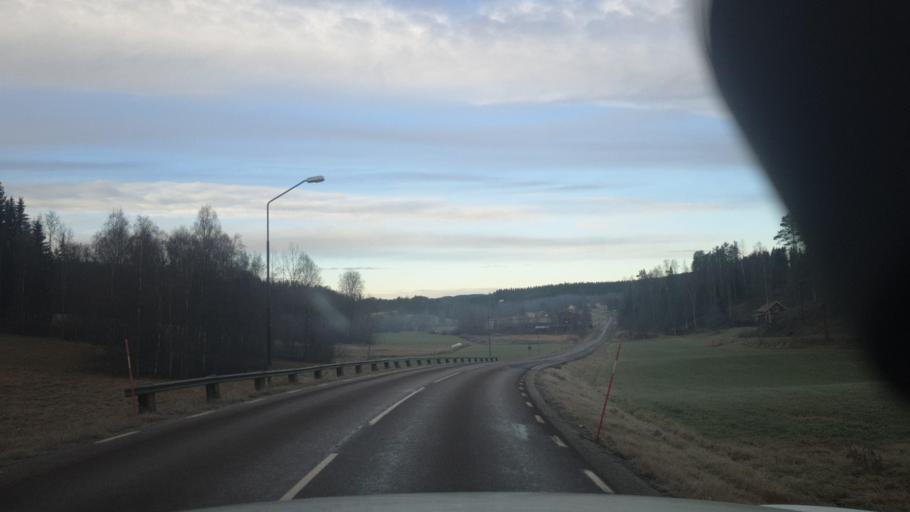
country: SE
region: Vaermland
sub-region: Arvika Kommun
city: Arvika
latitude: 59.8491
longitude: 12.5482
